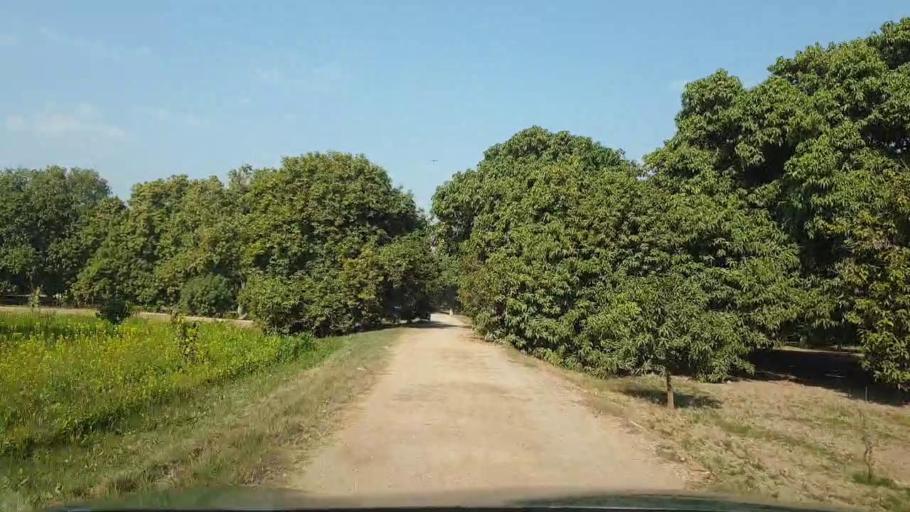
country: PK
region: Sindh
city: Tando Allahyar
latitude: 25.4666
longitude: 68.6273
